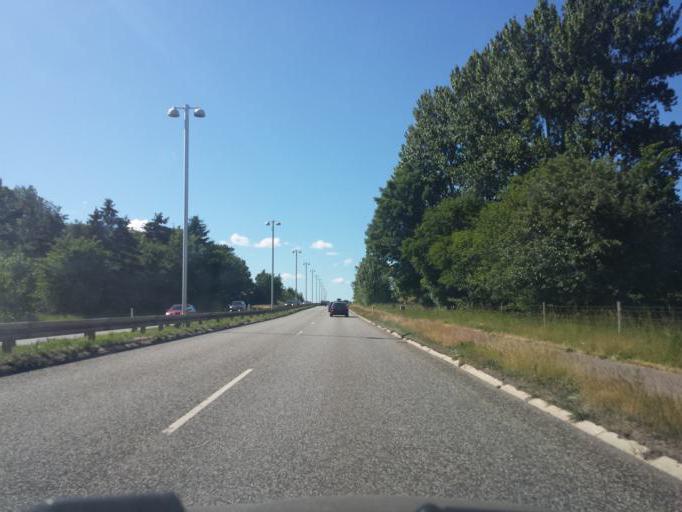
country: DK
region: Capital Region
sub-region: Ballerup Kommune
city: Malov
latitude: 55.7424
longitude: 12.3356
